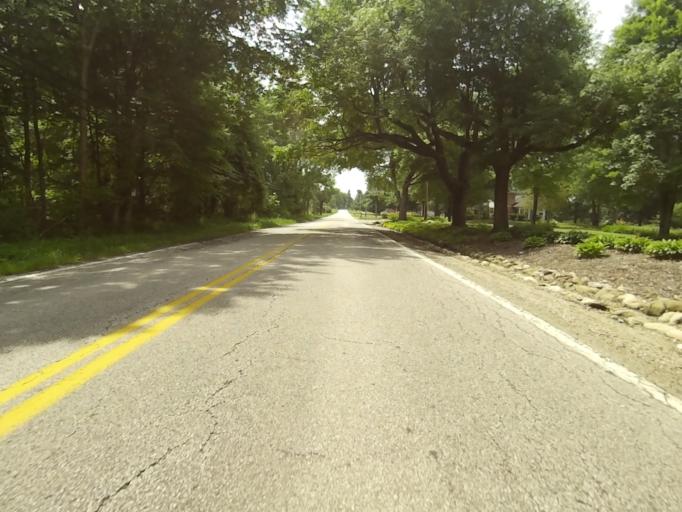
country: US
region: Ohio
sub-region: Portage County
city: Kent
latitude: 41.1776
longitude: -81.3659
